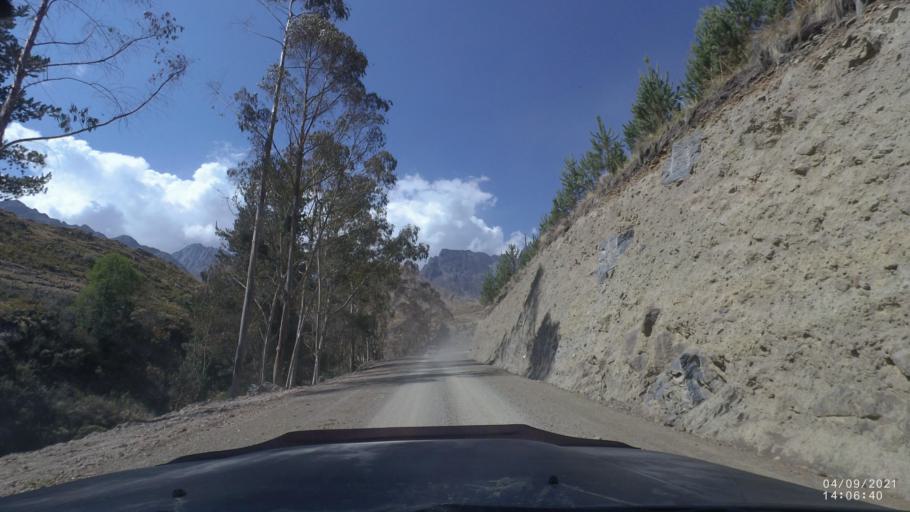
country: BO
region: Cochabamba
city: Sipe Sipe
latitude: -17.2298
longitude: -66.4702
